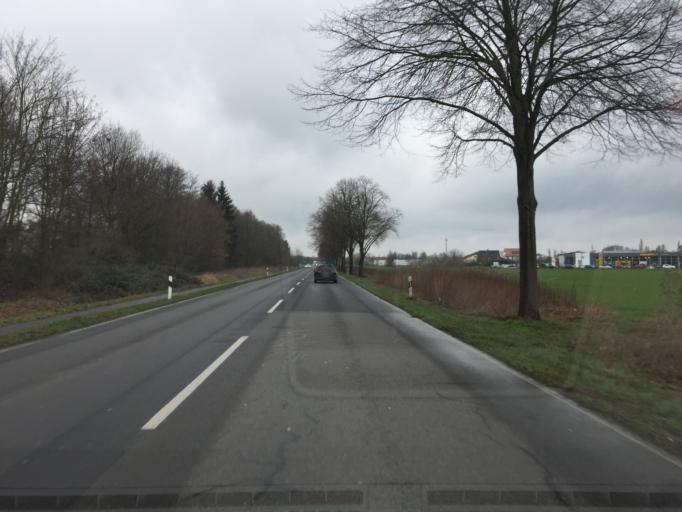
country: DE
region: Lower Saxony
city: Wunstorf
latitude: 52.4074
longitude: 9.4572
